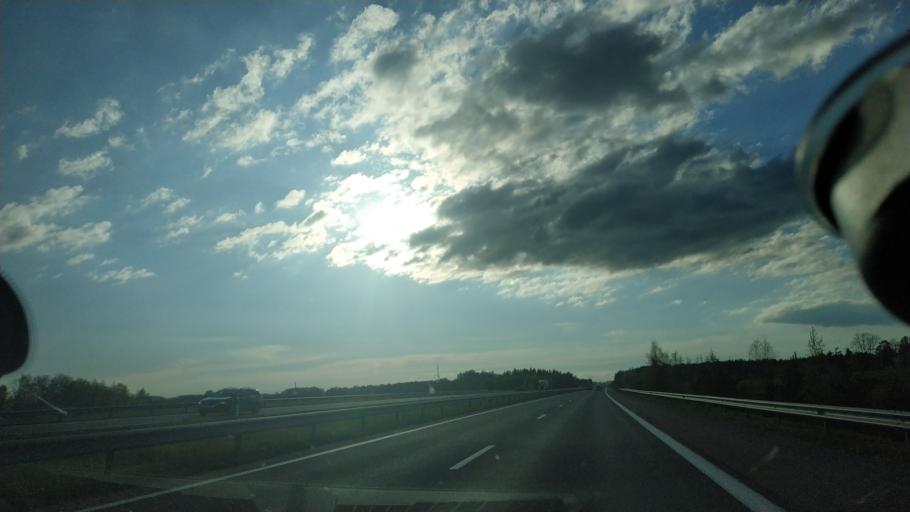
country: LT
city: Raseiniai
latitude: 55.3897
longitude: 22.8898
